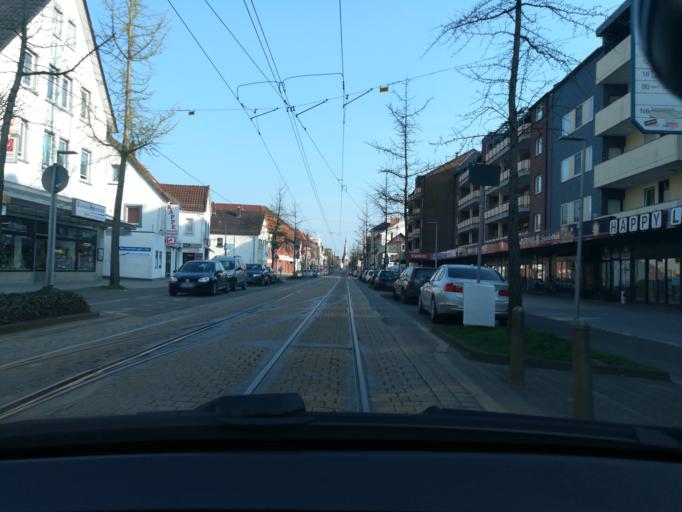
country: DE
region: North Rhine-Westphalia
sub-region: Regierungsbezirk Detmold
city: Bielefeld
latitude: 51.9938
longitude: 8.5069
